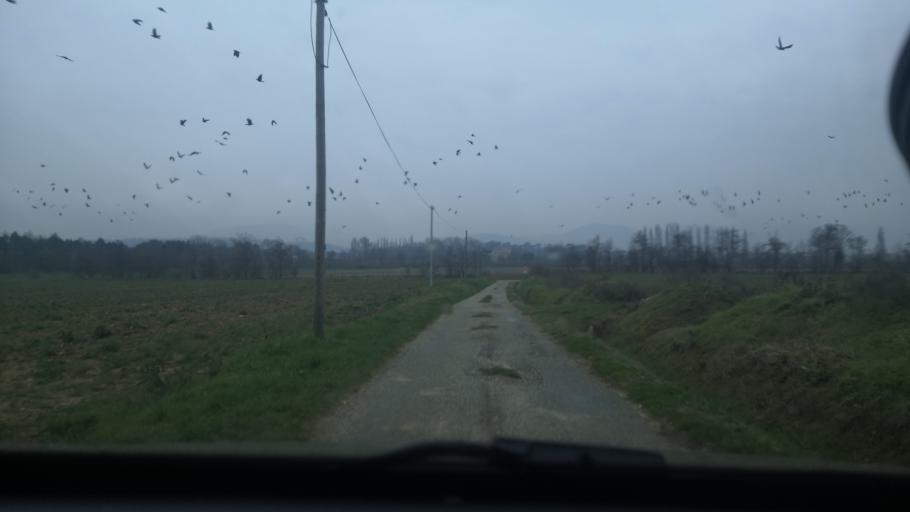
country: FR
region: Rhone-Alpes
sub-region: Departement de la Drome
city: Montboucher-sur-Jabron
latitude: 44.5605
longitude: 4.8143
